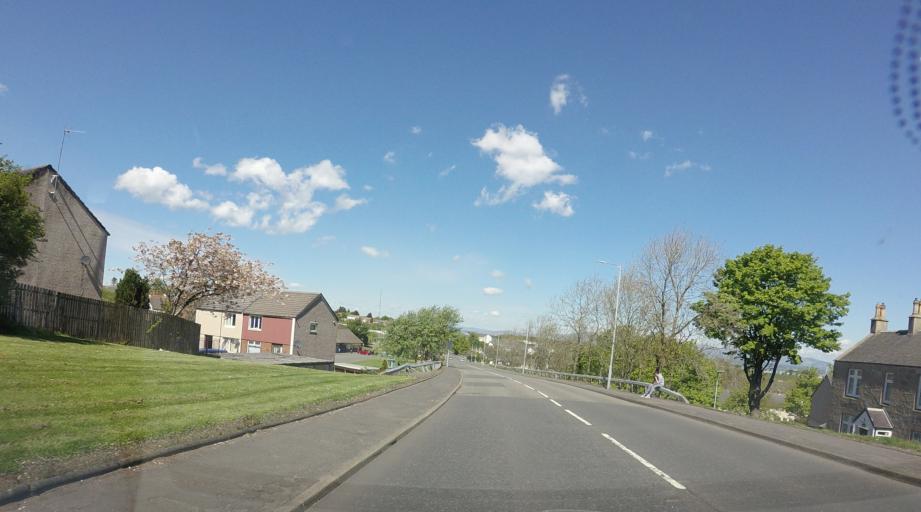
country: GB
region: Scotland
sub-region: Falkirk
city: Polmont
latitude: 55.9684
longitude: -3.6959
